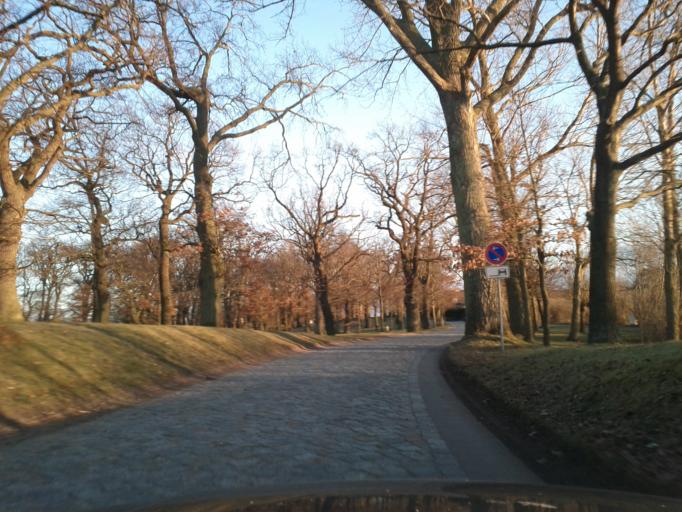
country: DE
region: Mecklenburg-Vorpommern
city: Blowatz
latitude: 54.0128
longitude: 11.4308
